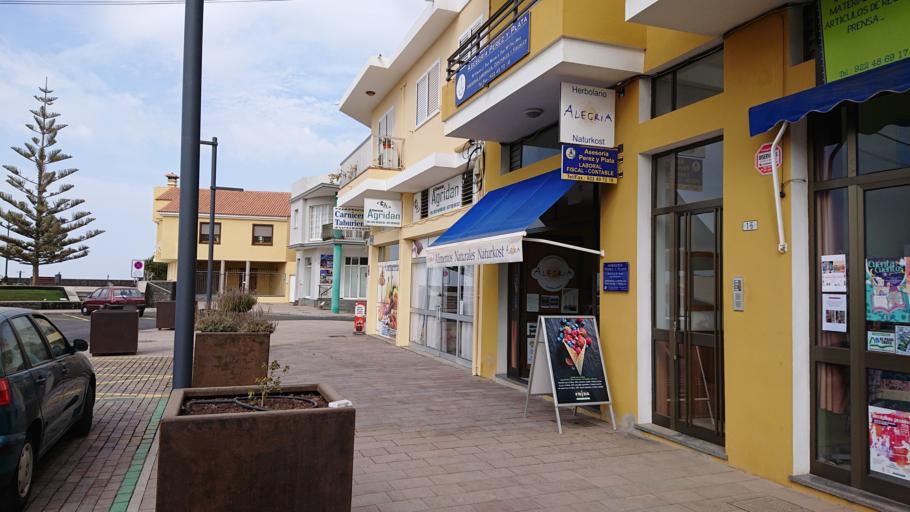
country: ES
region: Canary Islands
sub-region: Provincia de Santa Cruz de Tenerife
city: El Paso
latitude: 28.6527
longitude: -17.8815
